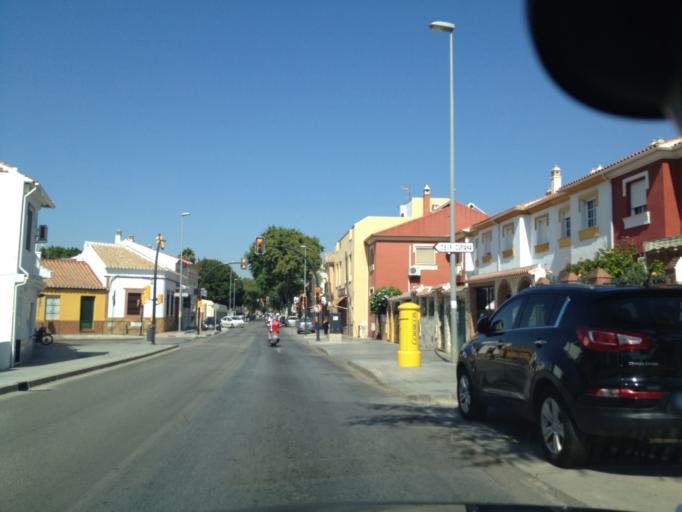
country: ES
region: Andalusia
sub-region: Provincia de Malaga
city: Alhaurin de la Torre
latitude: 36.7222
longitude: -4.5367
